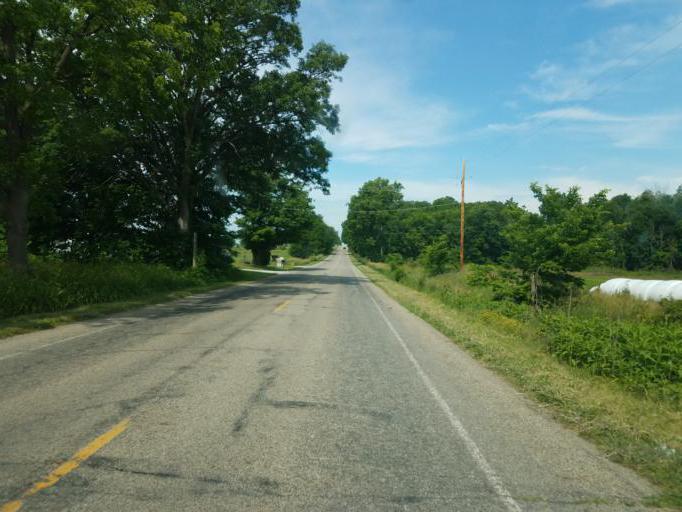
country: US
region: Michigan
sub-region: Barry County
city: Nashville
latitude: 42.6262
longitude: -84.9661
